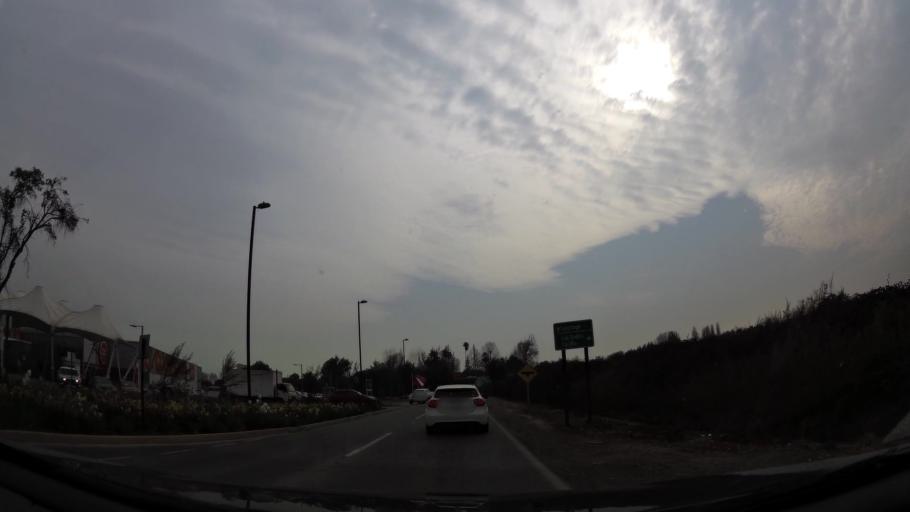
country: CL
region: Santiago Metropolitan
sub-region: Provincia de Chacabuco
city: Chicureo Abajo
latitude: -33.2855
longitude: -70.6993
